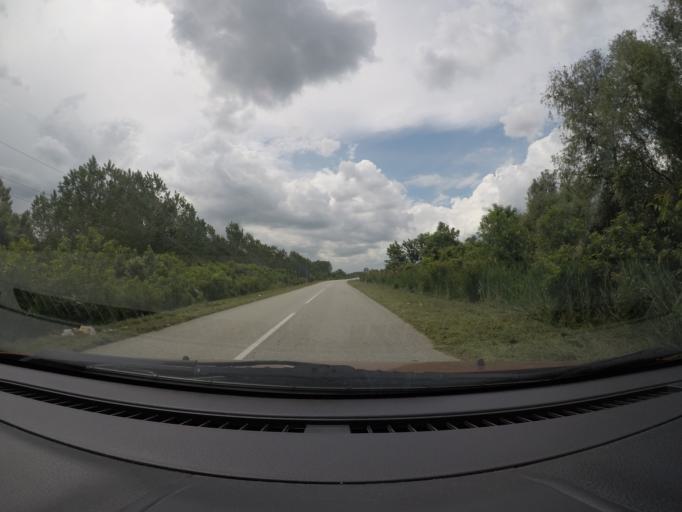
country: RS
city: Centa
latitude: 45.0958
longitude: 20.4099
